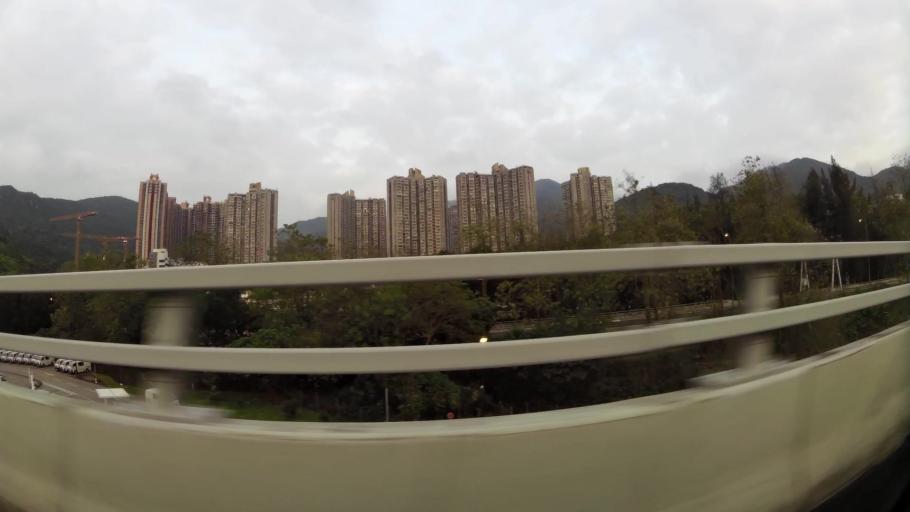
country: HK
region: Sha Tin
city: Sha Tin
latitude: 22.3813
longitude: 114.2104
